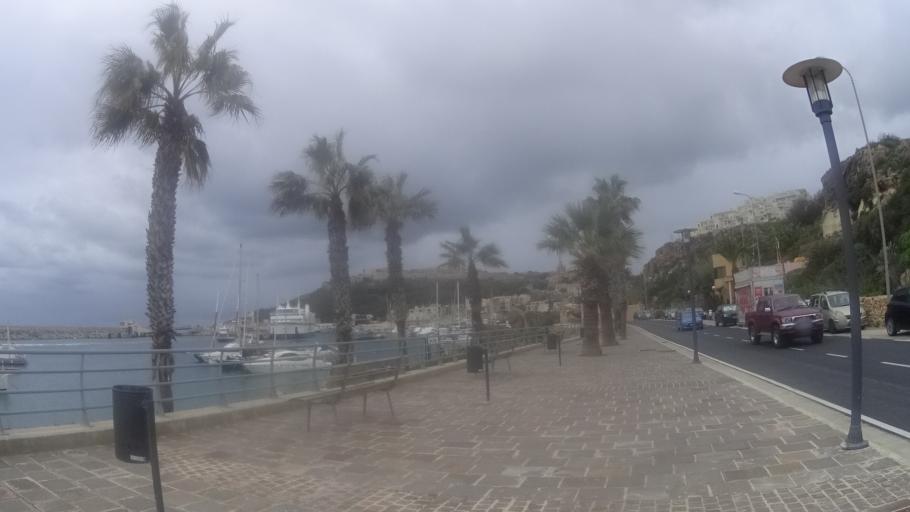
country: MT
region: Ghajnsielem
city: Mgarr
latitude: 36.0272
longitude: 14.3008
